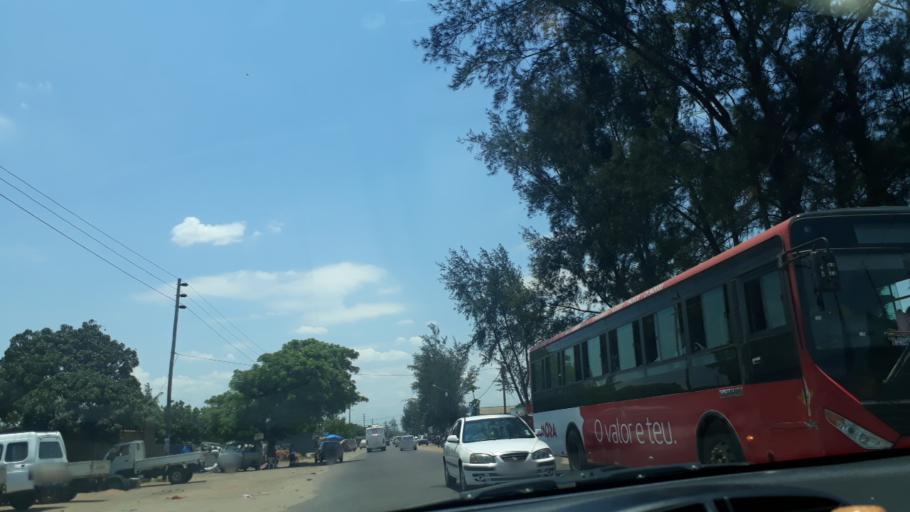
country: MZ
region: Maputo City
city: Maputo
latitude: -25.8974
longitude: 32.6001
